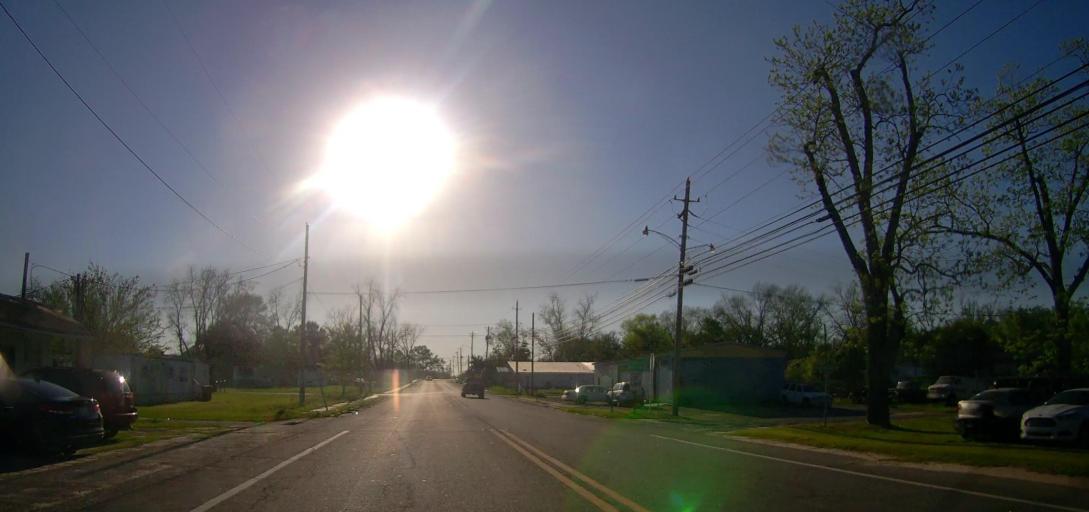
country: US
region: Georgia
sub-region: Ben Hill County
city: Fitzgerald
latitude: 31.7141
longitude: -83.2399
